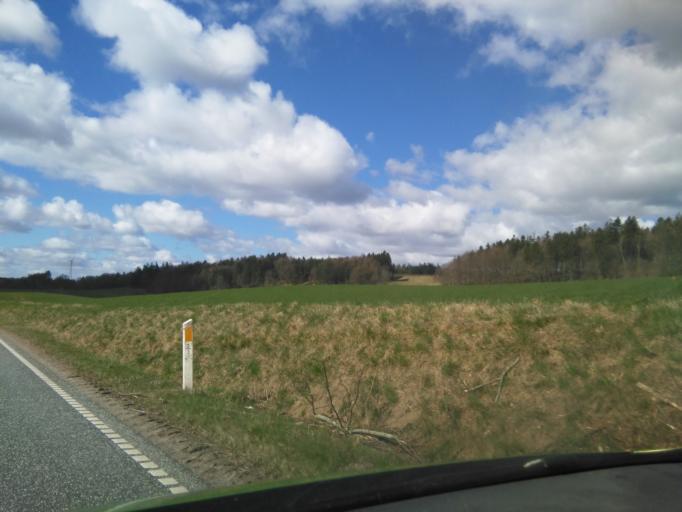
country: DK
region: Central Jutland
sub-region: Horsens Kommune
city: Braedstrup
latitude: 56.0260
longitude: 9.5570
